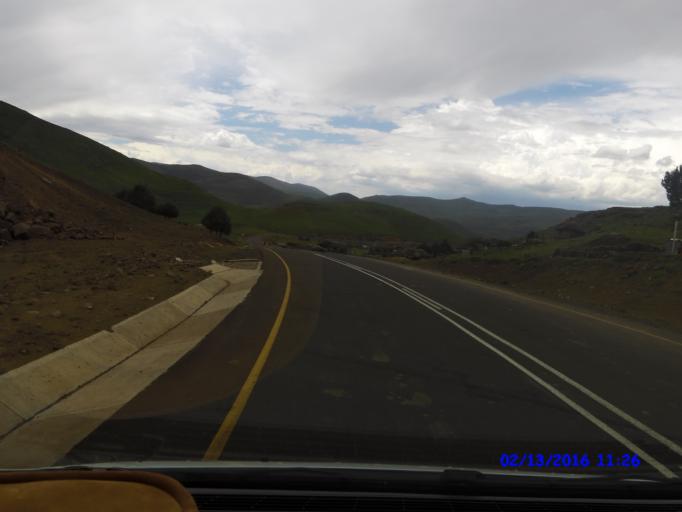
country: LS
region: Maseru
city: Nako
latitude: -29.7697
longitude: 28.0136
